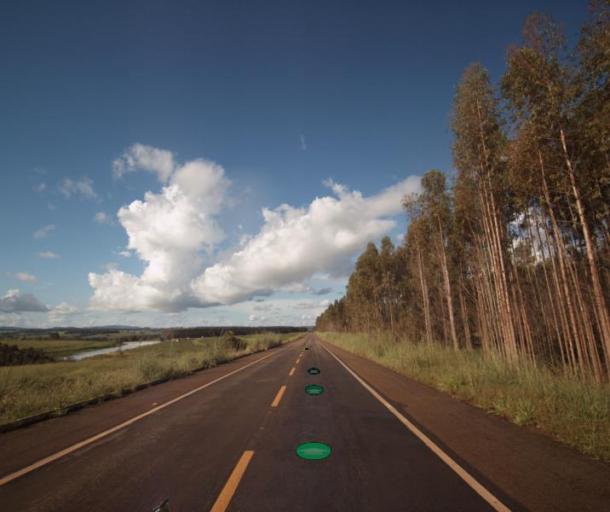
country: BR
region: Goias
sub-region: Itaberai
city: Itaberai
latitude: -16.0119
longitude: -49.7662
